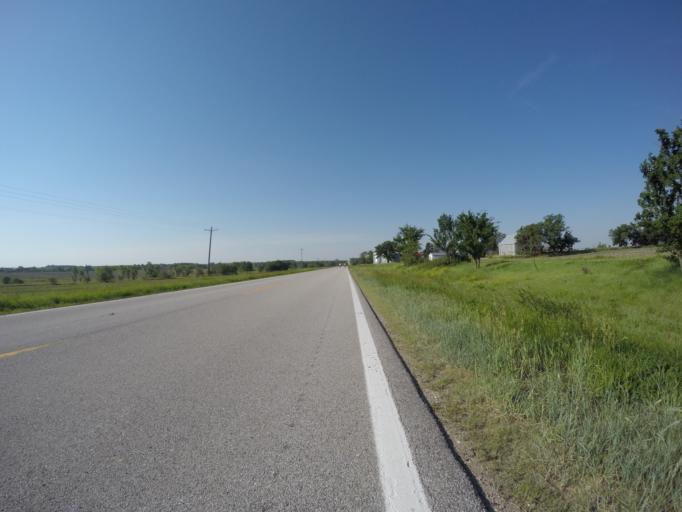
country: US
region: Nebraska
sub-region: Gage County
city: Wymore
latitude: 40.0502
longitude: -96.4828
